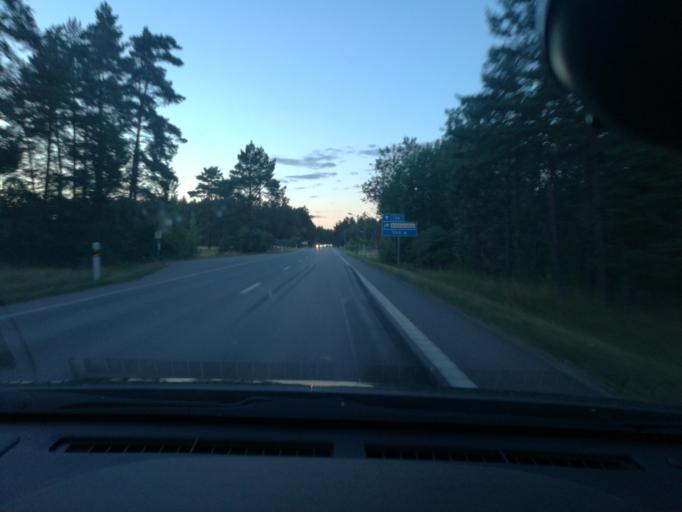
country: SE
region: Kalmar
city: Faerjestaden
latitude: 56.7594
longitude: 16.5582
